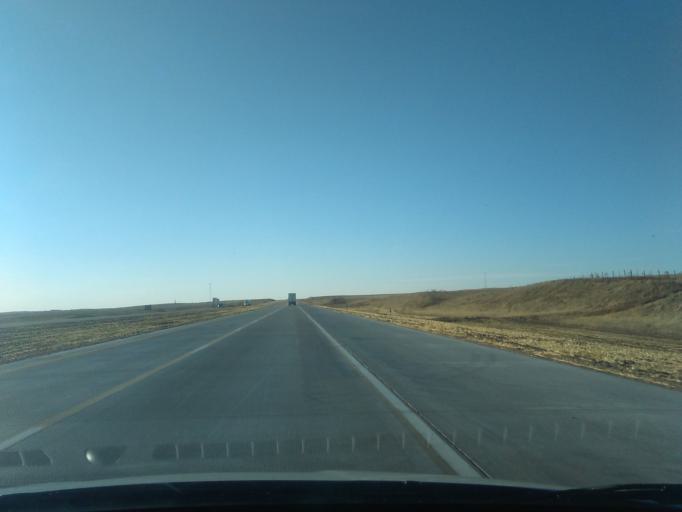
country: US
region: Nebraska
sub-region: Deuel County
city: Chappell
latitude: 41.1137
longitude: -102.6493
